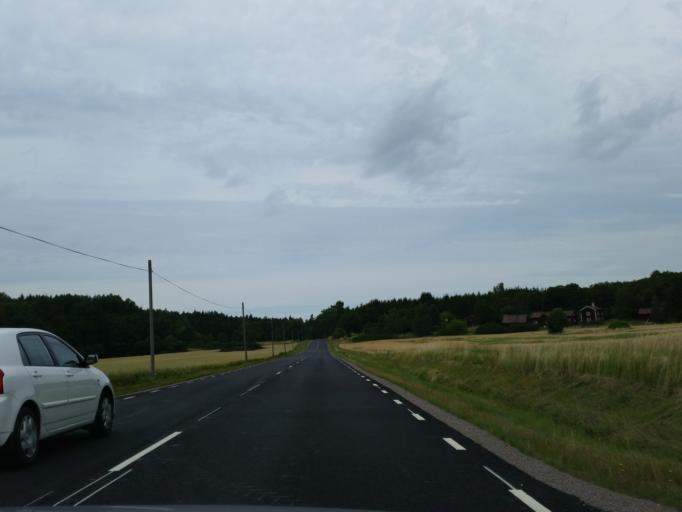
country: SE
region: Soedermanland
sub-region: Strangnas Kommun
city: Mariefred
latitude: 59.2589
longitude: 17.1716
